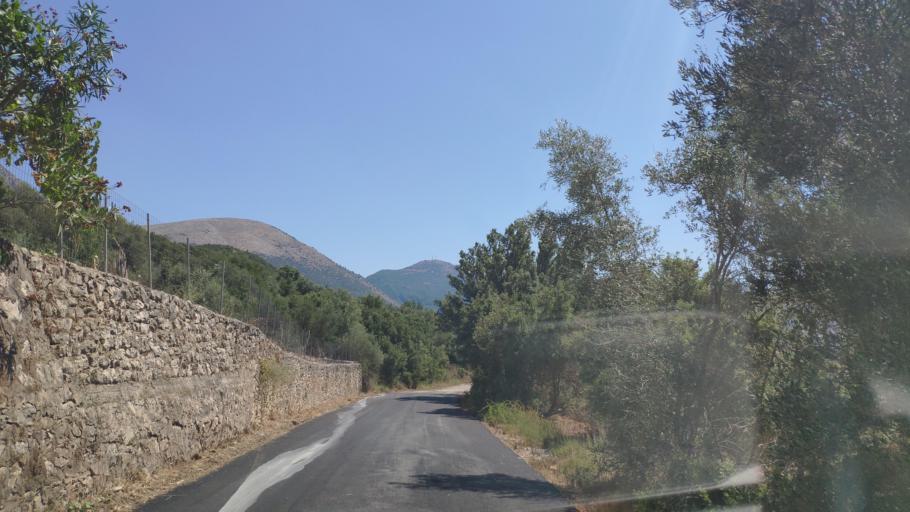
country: GR
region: Epirus
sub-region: Nomos Prevezis
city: Kanalaki
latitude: 39.2731
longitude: 20.5998
